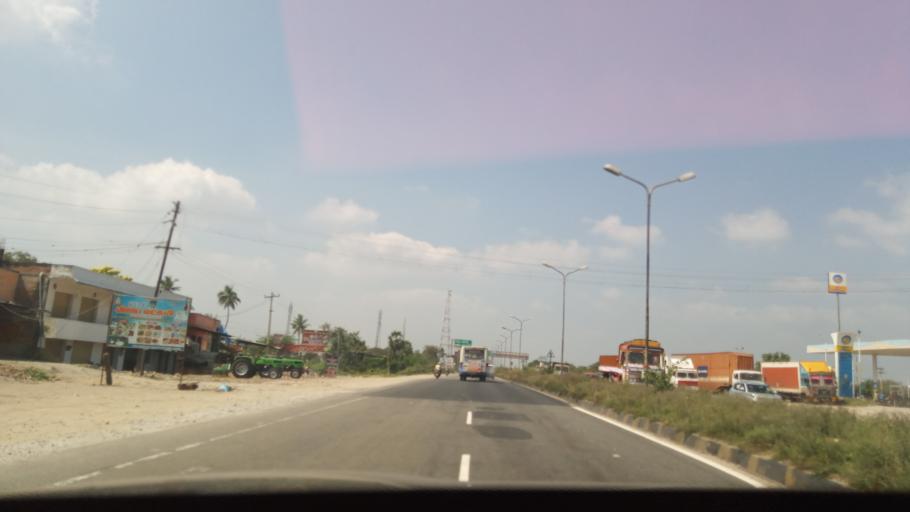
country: IN
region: Tamil Nadu
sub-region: Vellore
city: Walajapet
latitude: 12.9088
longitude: 79.4085
